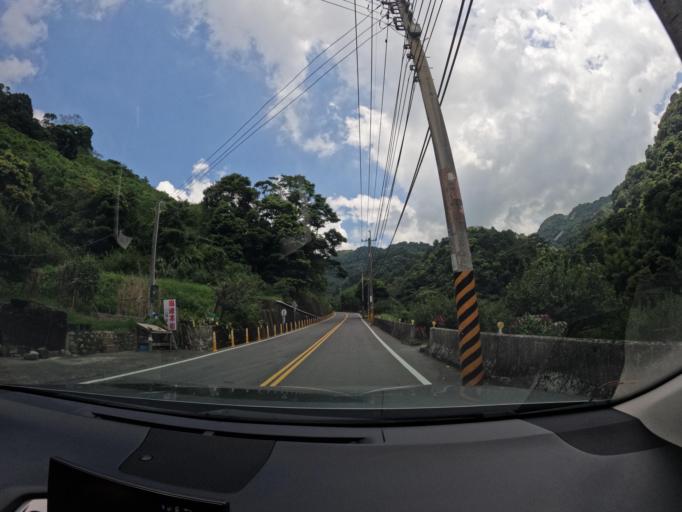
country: TW
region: Taiwan
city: Fengyuan
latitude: 24.3828
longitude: 120.8117
